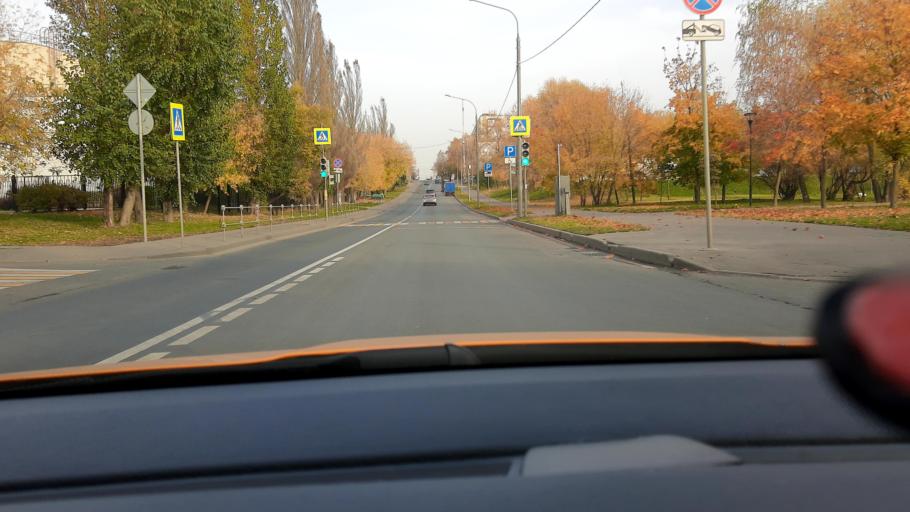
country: RU
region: Moscow
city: Vagonoremont
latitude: 55.8982
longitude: 37.5352
